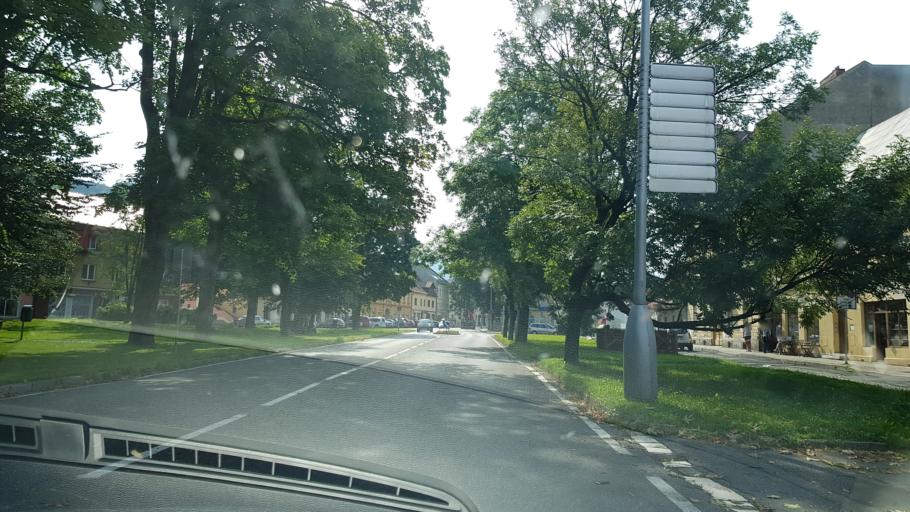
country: CZ
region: Olomoucky
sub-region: Okres Jesenik
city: Jesenik
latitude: 50.2274
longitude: 17.2047
